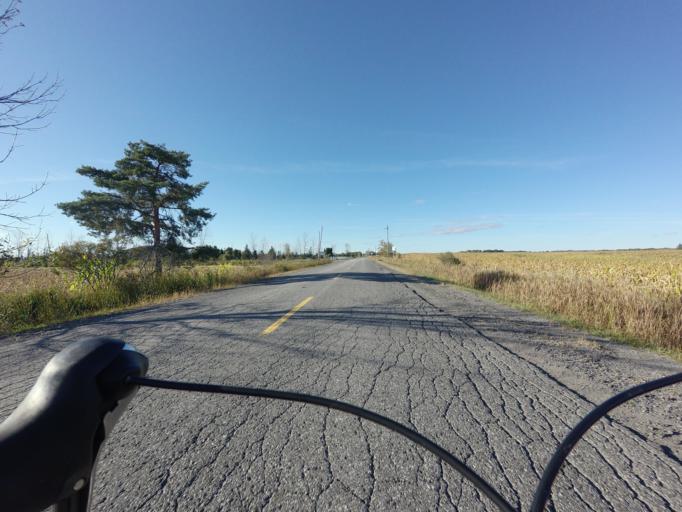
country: CA
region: Ontario
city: Bells Corners
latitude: 45.2031
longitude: -75.7920
